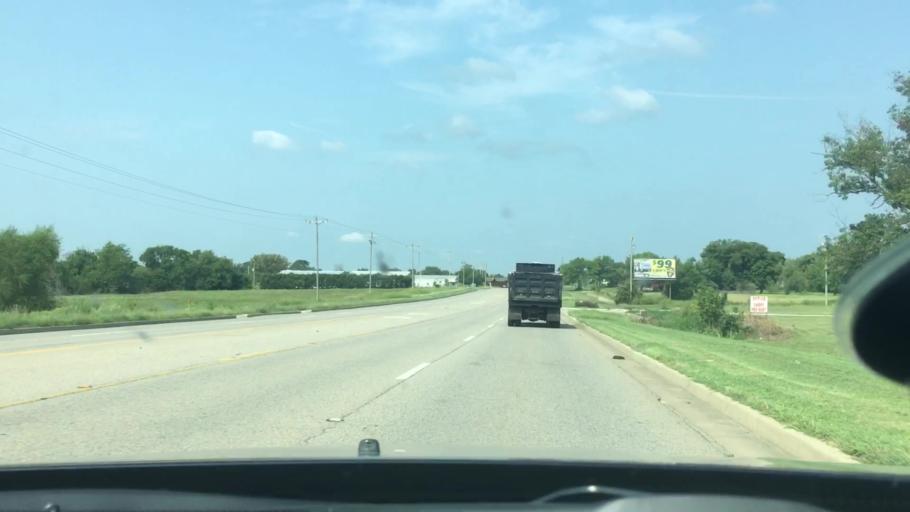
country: US
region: Oklahoma
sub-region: Bryan County
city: Calera
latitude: 33.9982
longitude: -96.5145
